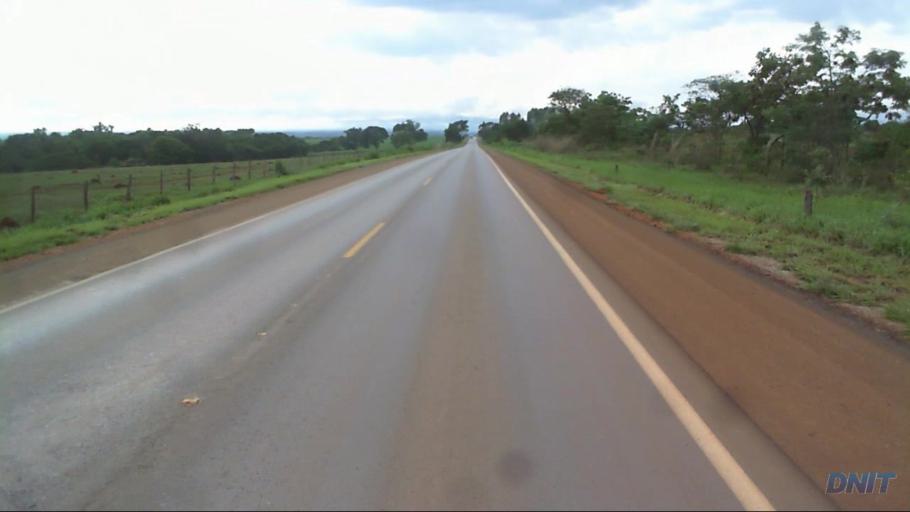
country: BR
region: Goias
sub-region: Uruacu
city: Uruacu
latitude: -14.7075
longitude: -49.1122
